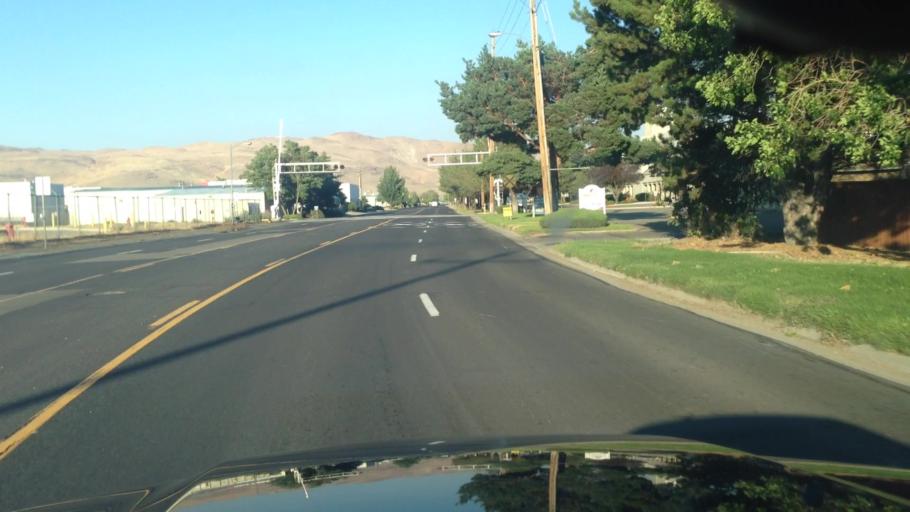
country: US
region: Nevada
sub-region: Washoe County
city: Sparks
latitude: 39.5212
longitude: -119.7330
